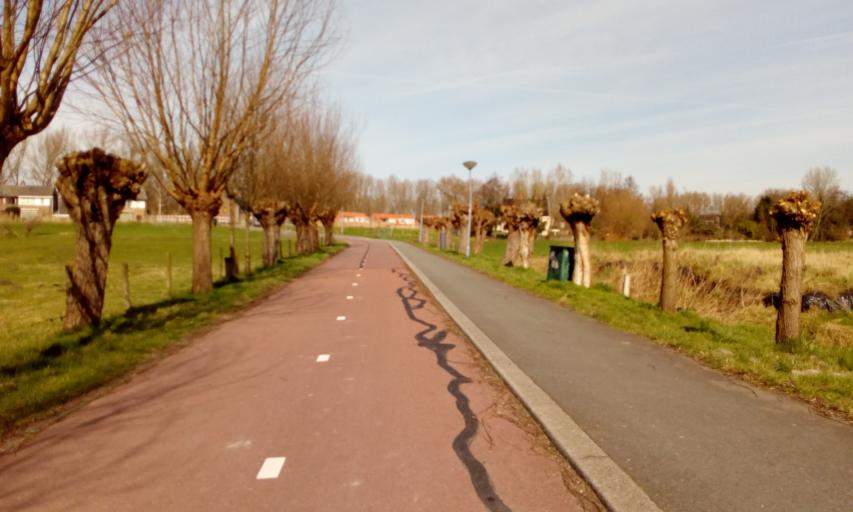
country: NL
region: South Holland
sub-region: Gemeente Lansingerland
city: Bergschenhoek
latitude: 51.9646
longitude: 4.5288
